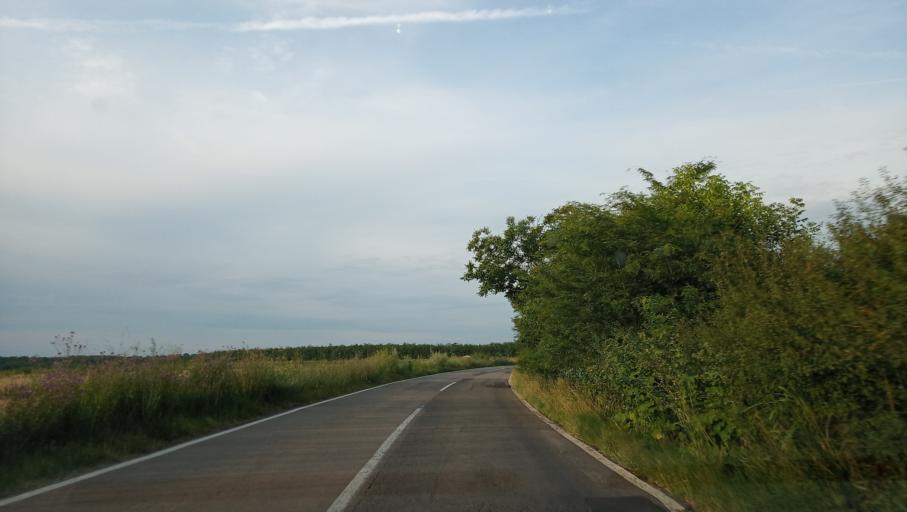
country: RO
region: Giurgiu
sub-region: Comuna Hotarele
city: Hotarele
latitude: 44.1277
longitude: 26.3869
